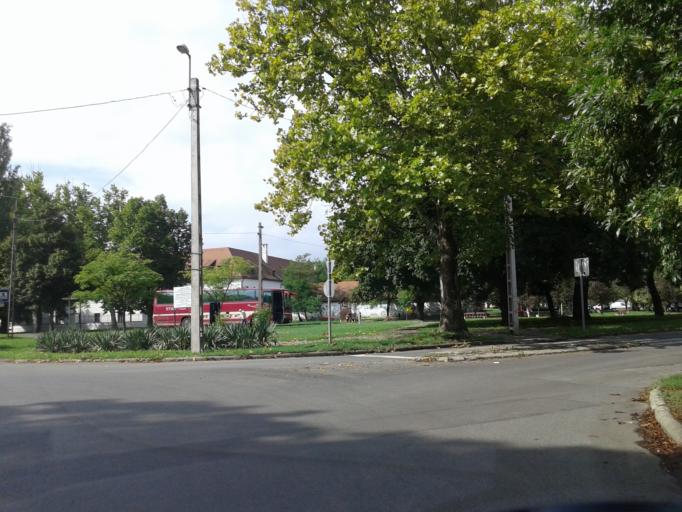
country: HU
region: Csongrad
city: Szeged
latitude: 46.2420
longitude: 20.1379
